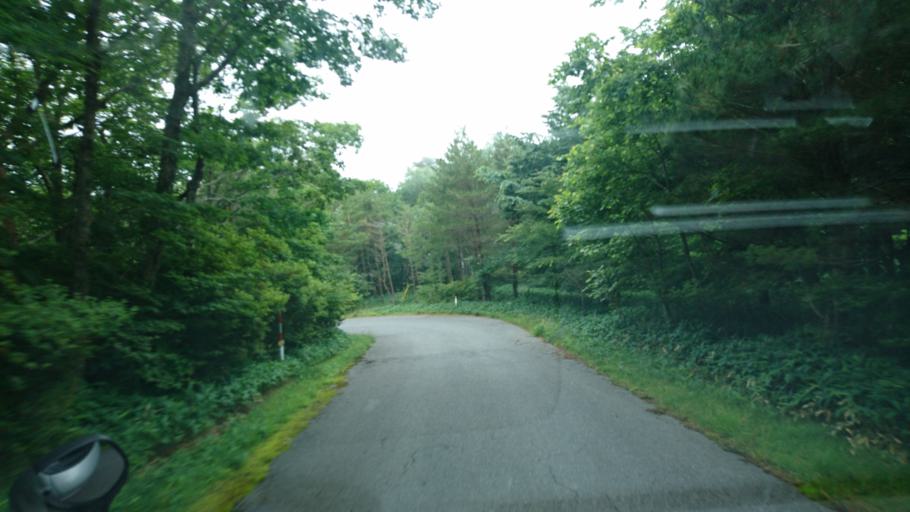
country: JP
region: Iwate
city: Ofunato
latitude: 39.1465
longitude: 141.7543
